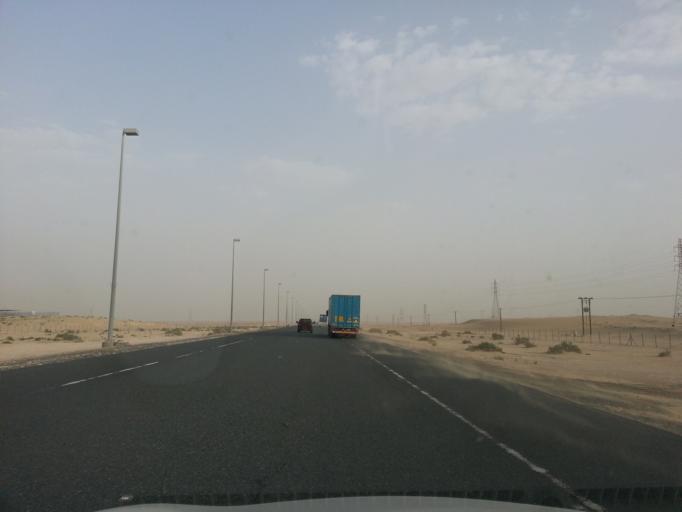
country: AE
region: Dubai
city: Dubai
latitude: 24.7491
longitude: 55.1059
